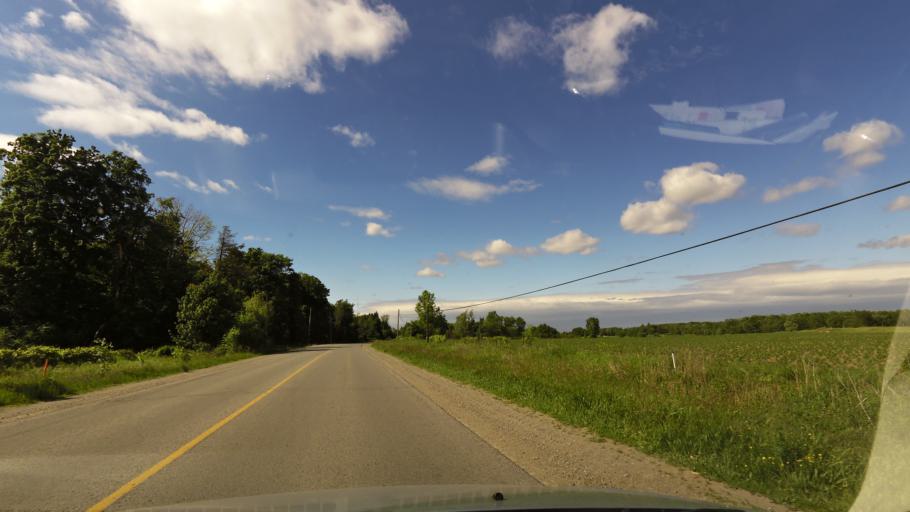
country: CA
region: Ontario
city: Bradford West Gwillimbury
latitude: 44.1583
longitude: -79.6149
